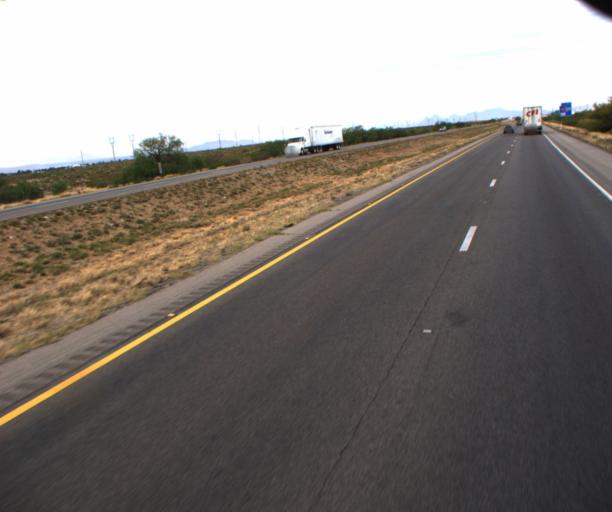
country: US
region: Arizona
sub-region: Pima County
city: Vail
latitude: 32.0485
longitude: -110.7527
